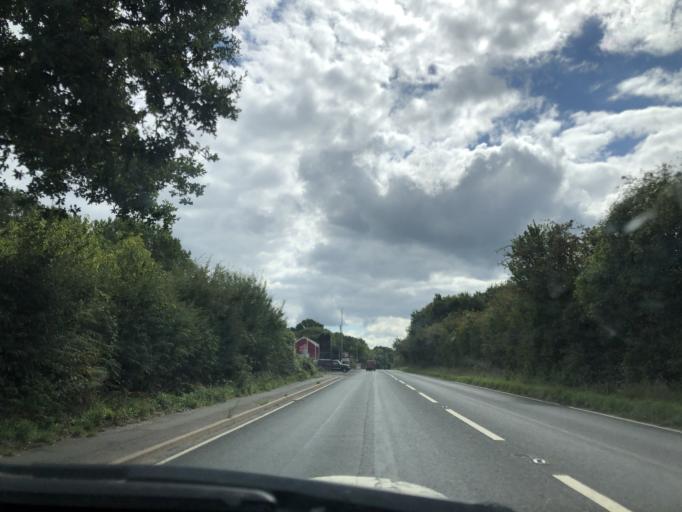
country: GB
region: England
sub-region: Kent
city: Halstead
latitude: 51.3256
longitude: 0.1543
